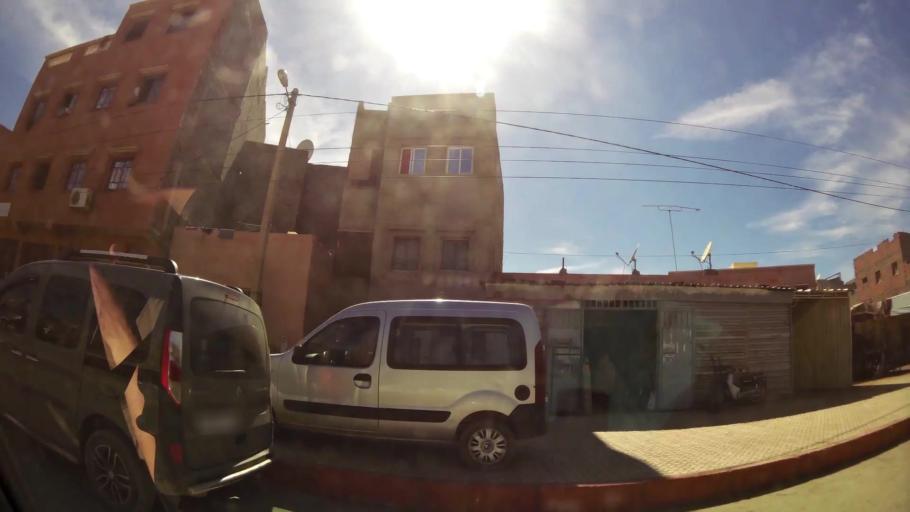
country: MA
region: Marrakech-Tensift-Al Haouz
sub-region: Marrakech
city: Marrakesh
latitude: 31.6800
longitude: -8.0169
